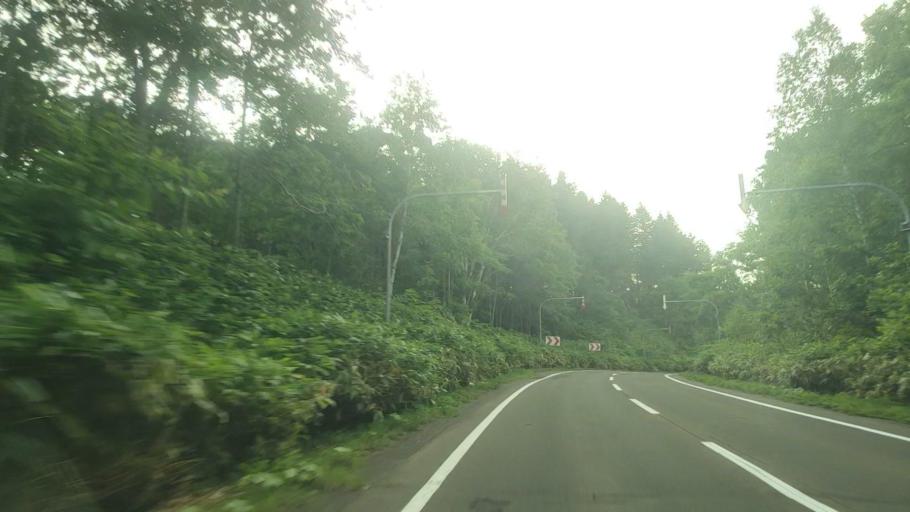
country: JP
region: Hokkaido
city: Bibai
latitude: 43.1415
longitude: 142.0923
